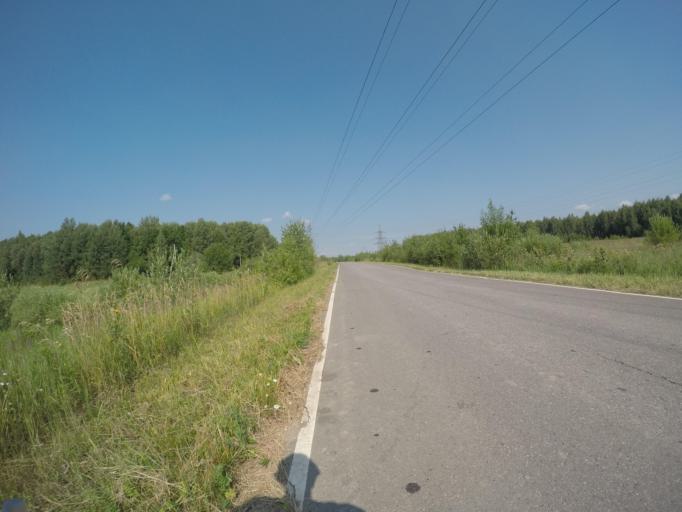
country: RU
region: Moskovskaya
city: Rechitsy
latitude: 55.6258
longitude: 38.5208
